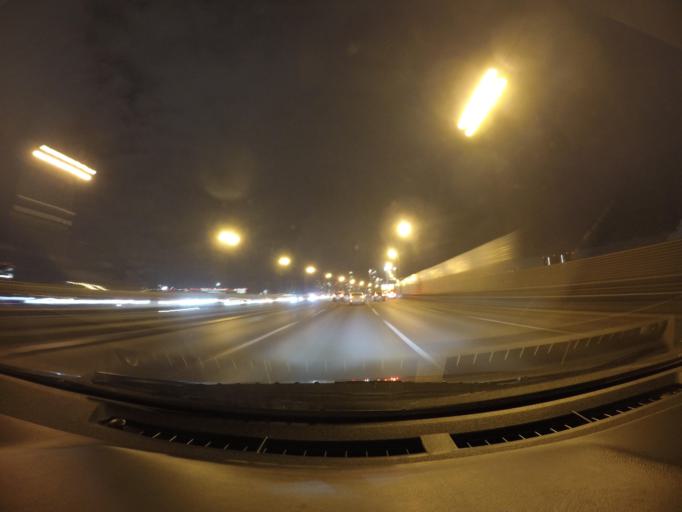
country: RU
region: Moscow
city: Lefortovo
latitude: 55.7414
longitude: 37.6974
